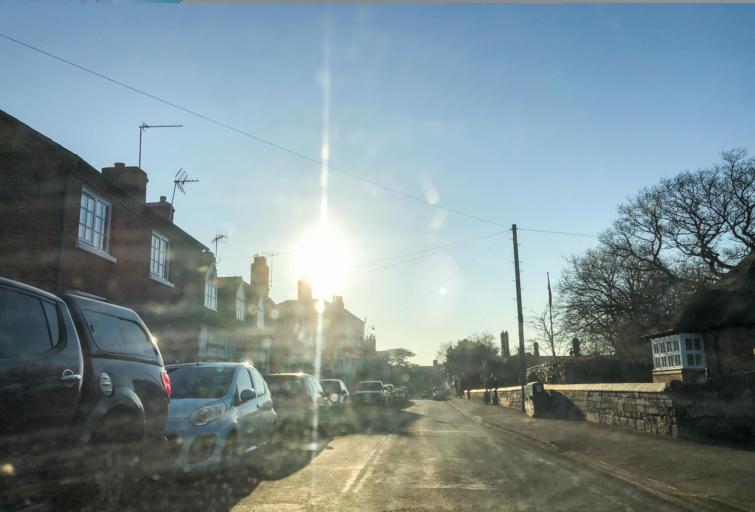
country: GB
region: England
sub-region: Warwickshire
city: Warwick
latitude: 52.2450
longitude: -1.6048
